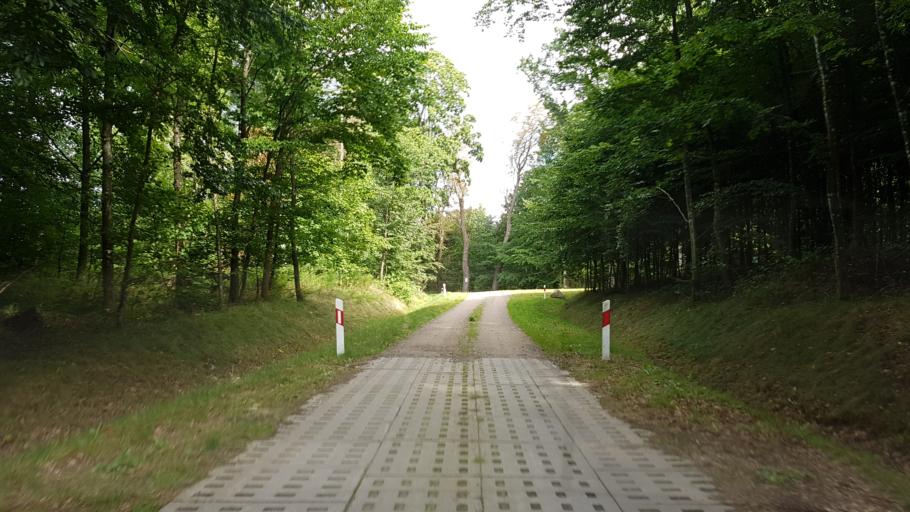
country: PL
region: West Pomeranian Voivodeship
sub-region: Powiat bialogardzki
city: Tychowo
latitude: 53.9792
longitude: 16.3876
